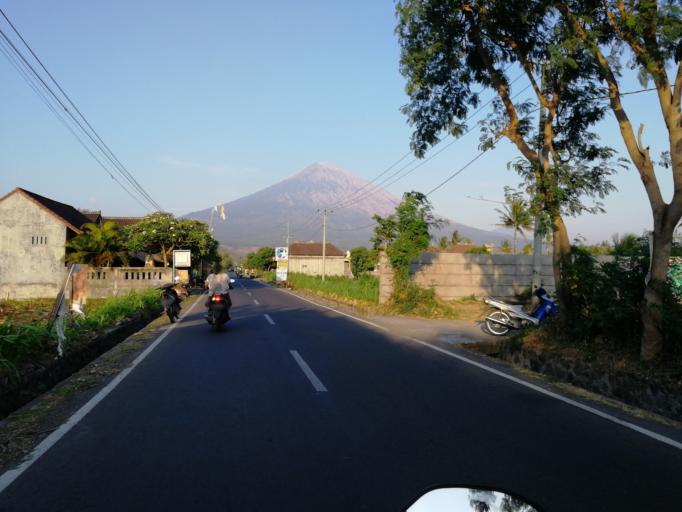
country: ID
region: Bali
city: Biaslantang Kaler
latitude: -8.3342
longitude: 115.6388
